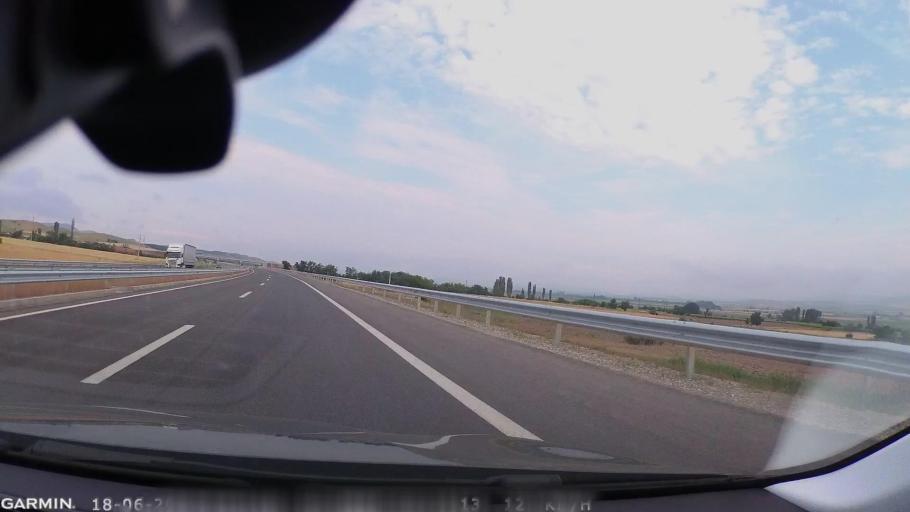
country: MK
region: Stip
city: Shtip
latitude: 41.7891
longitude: 22.1120
